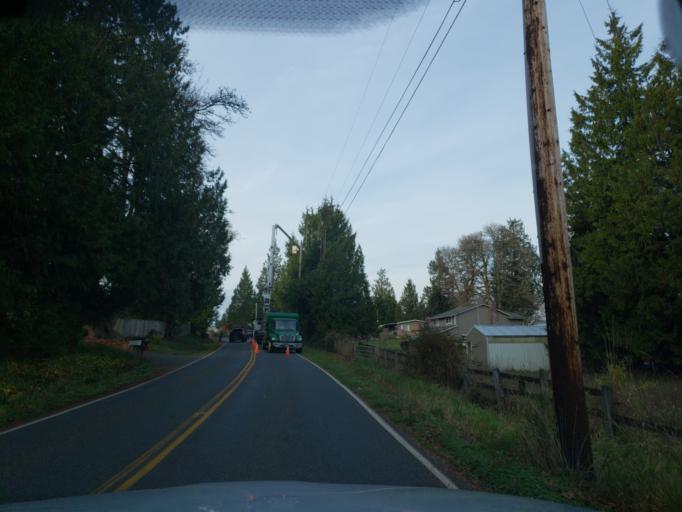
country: US
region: Washington
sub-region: Snohomish County
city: Cathcart
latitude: 47.8640
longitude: -122.0942
